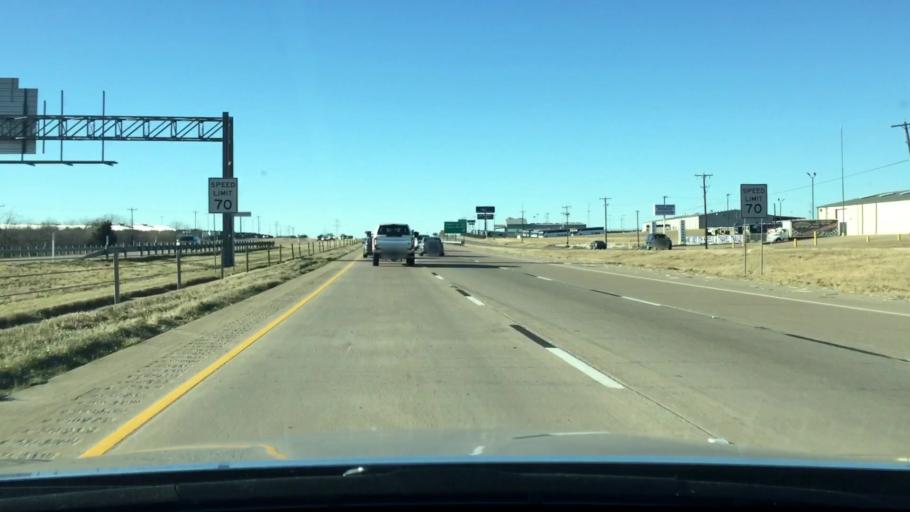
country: US
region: Texas
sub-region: Johnson County
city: Alvarado
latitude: 32.4244
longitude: -97.2319
